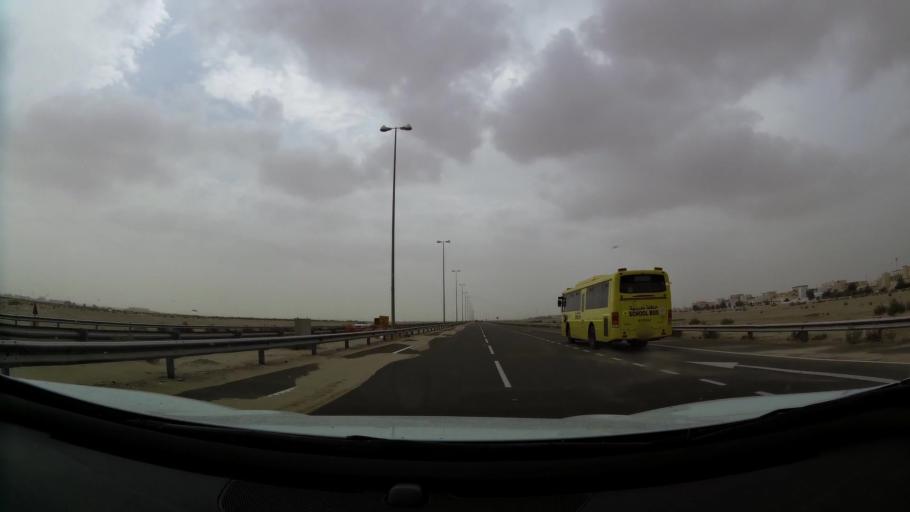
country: AE
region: Abu Dhabi
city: Abu Dhabi
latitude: 24.3683
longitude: 54.6711
